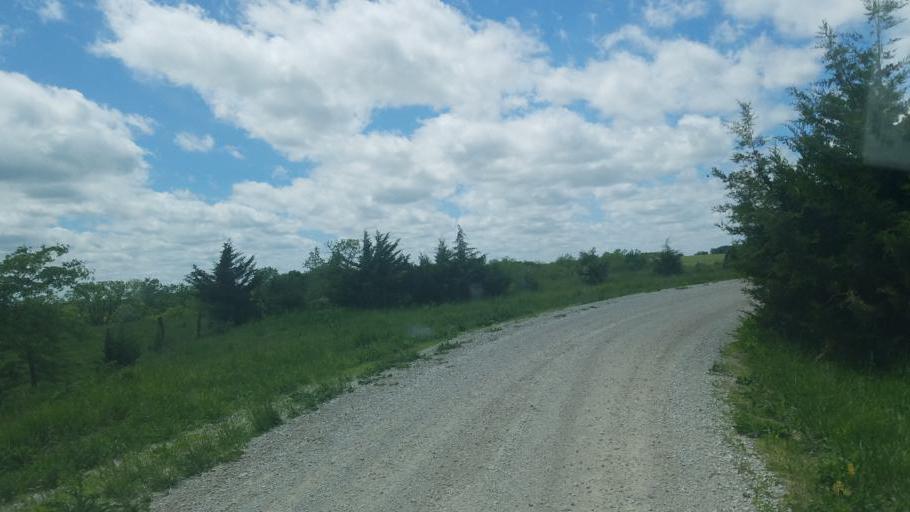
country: US
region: Iowa
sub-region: Decatur County
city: Lamoni
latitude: 40.5078
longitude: -94.0224
